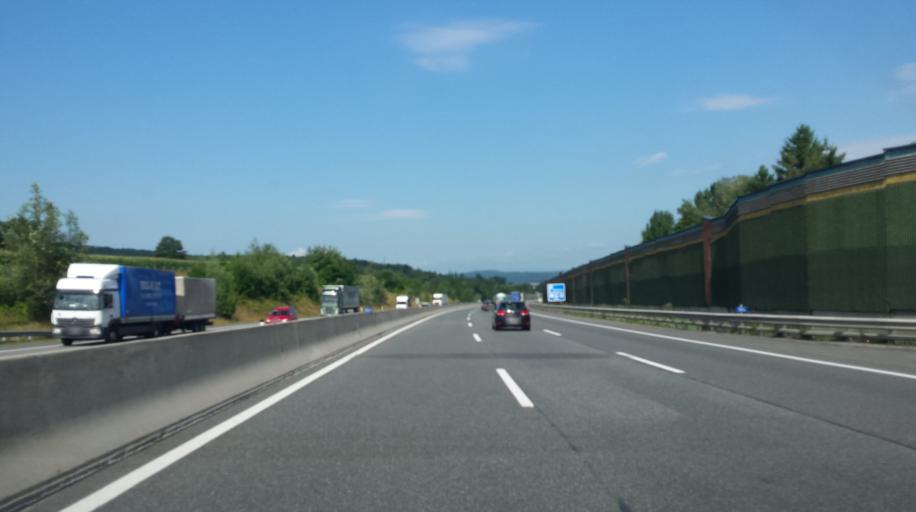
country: AT
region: Lower Austria
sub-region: Politischer Bezirk Sankt Polten
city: Kirchstetten
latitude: 48.1784
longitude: 15.8268
